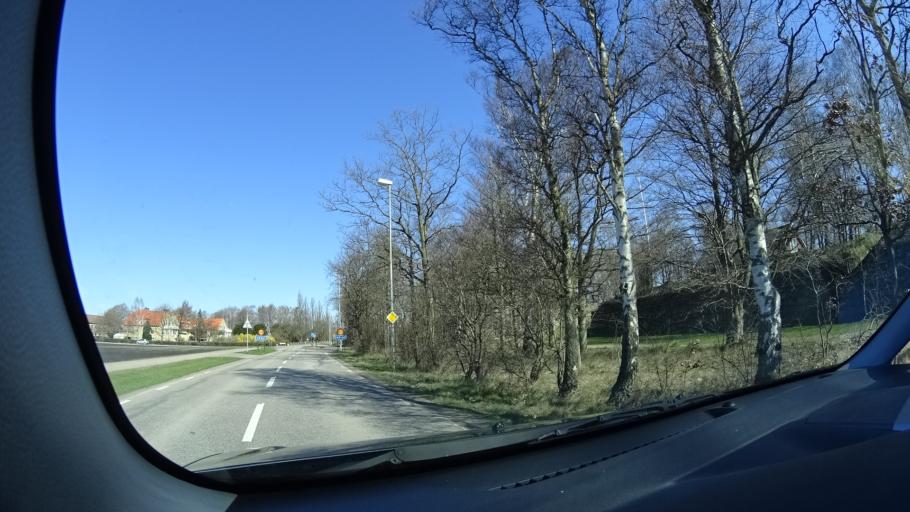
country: SE
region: Skane
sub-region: Hoganas Kommun
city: Hoganas
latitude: 56.2036
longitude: 12.5926
